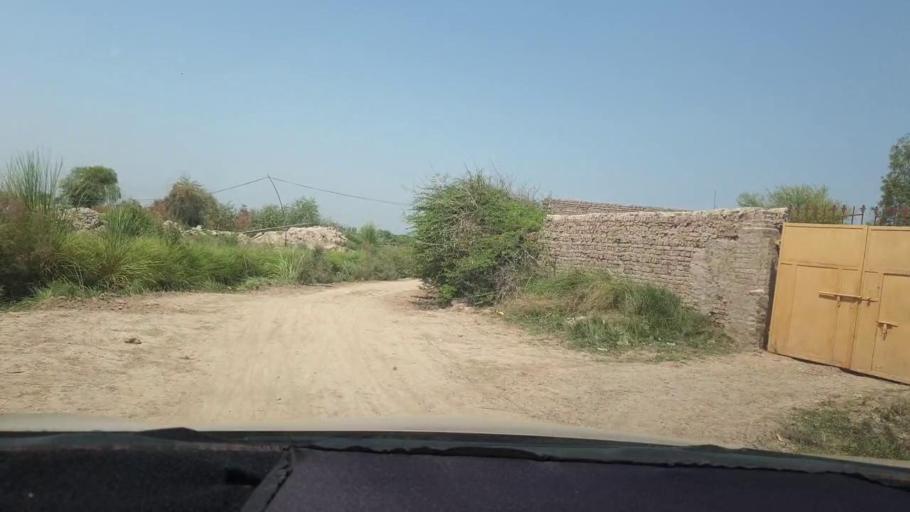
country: PK
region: Sindh
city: Shahdadkot
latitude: 27.8418
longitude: 67.8771
